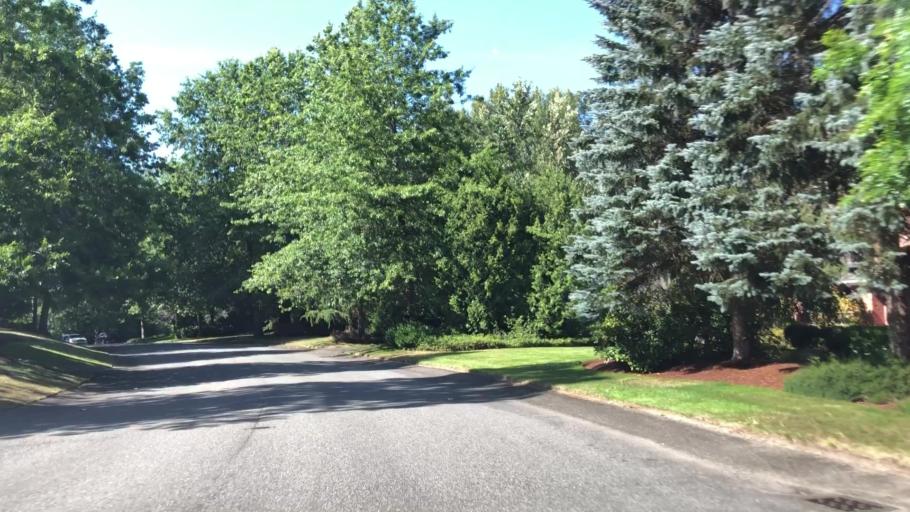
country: US
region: Washington
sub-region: King County
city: Cottage Lake
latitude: 47.7123
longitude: -122.0711
